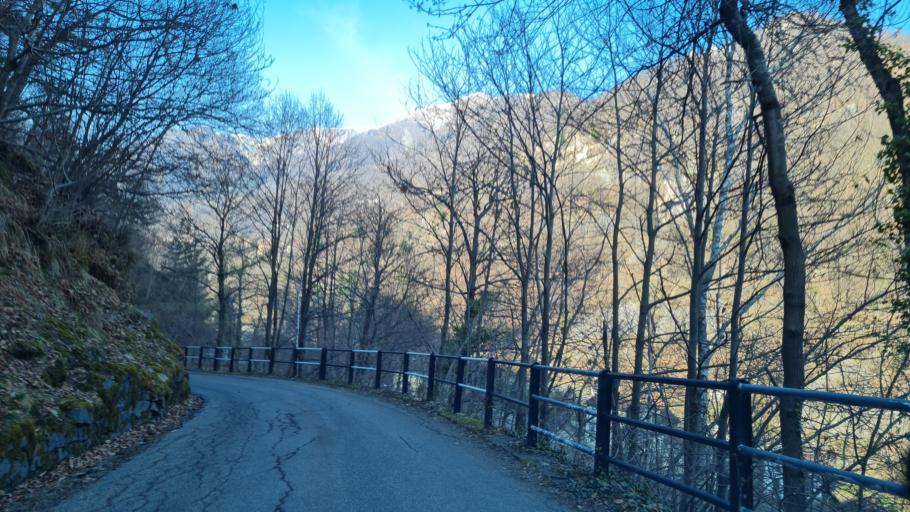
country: IT
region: Piedmont
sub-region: Provincia di Biella
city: San Paolo Cervo
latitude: 45.6457
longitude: 8.0168
